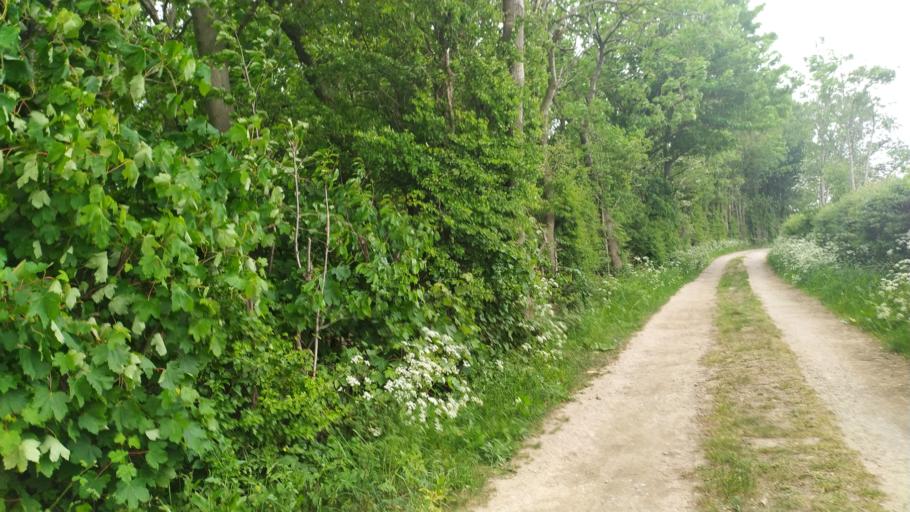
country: GB
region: England
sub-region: City and Borough of Leeds
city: Thorner
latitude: 53.8650
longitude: -1.3970
